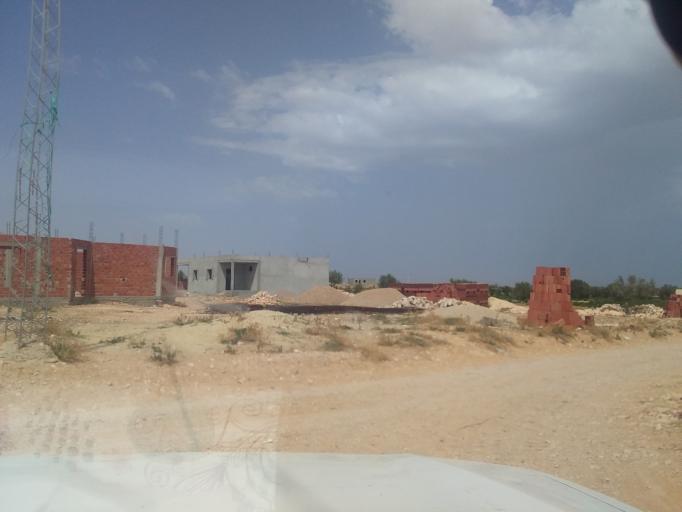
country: TN
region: Madanin
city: Medenine
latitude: 33.5886
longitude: 10.3240
